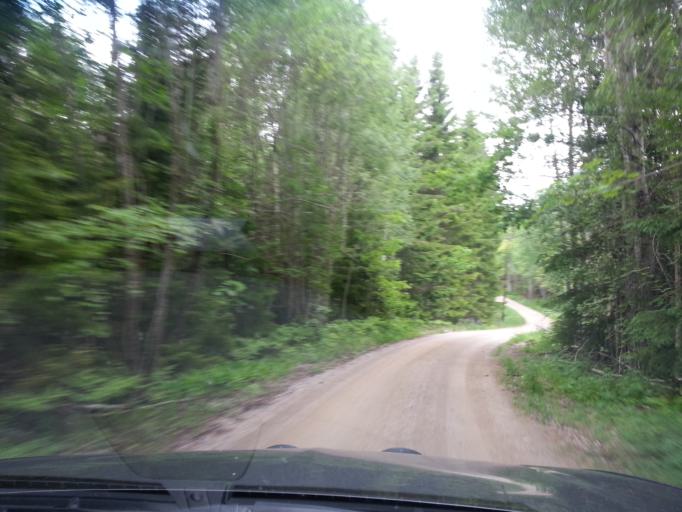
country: SE
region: Joenkoeping
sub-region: Vetlanda Kommun
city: Vetlanda
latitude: 57.2865
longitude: 15.1283
